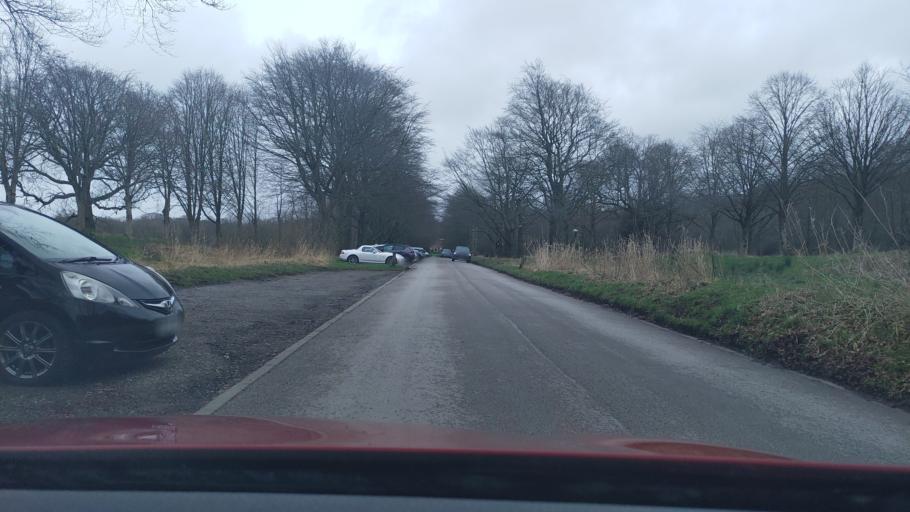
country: GB
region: England
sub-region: Borough of Bolton
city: Horwich
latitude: 53.6222
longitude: -2.5606
